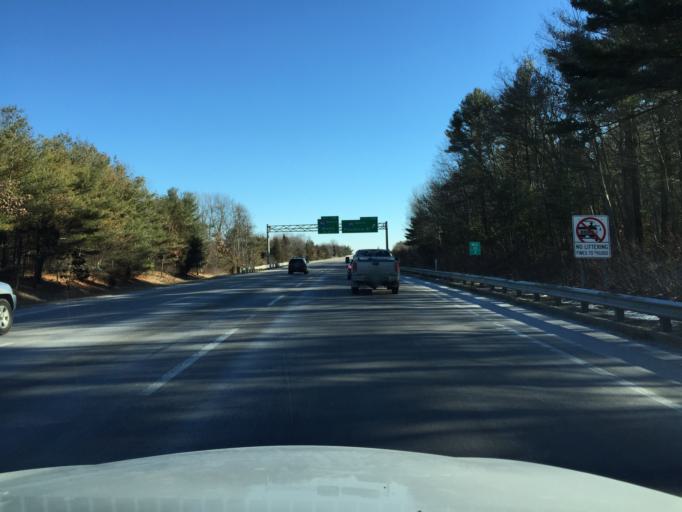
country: US
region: Massachusetts
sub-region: Norfolk County
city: Foxborough
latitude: 42.0291
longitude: -71.2633
